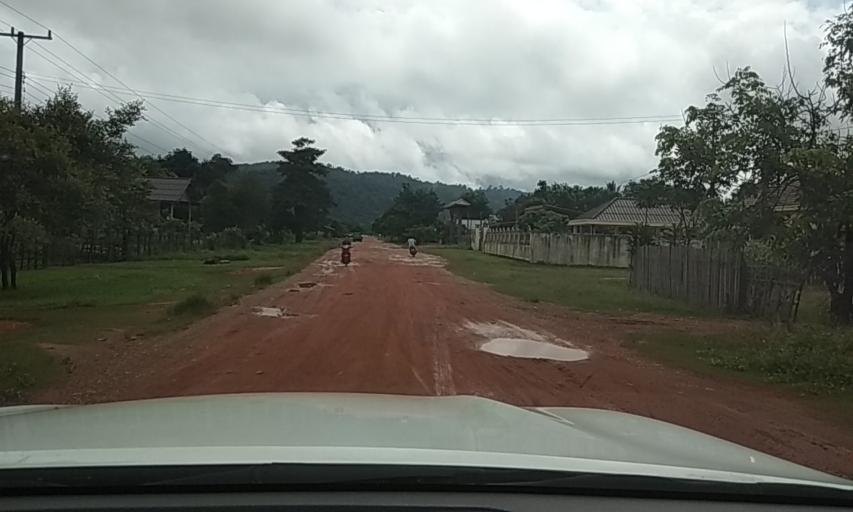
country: LA
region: Bolikhamxai
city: Bolikhan
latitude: 18.5571
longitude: 103.7333
